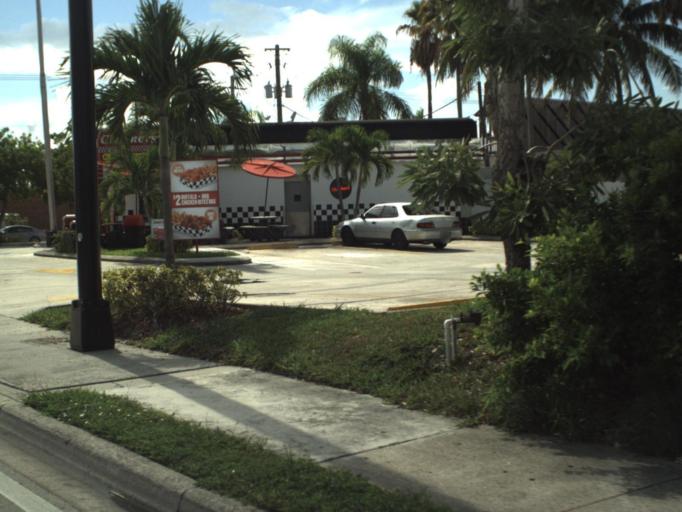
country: US
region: Florida
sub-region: Broward County
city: Wilton Manors
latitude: 26.1665
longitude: -80.1390
